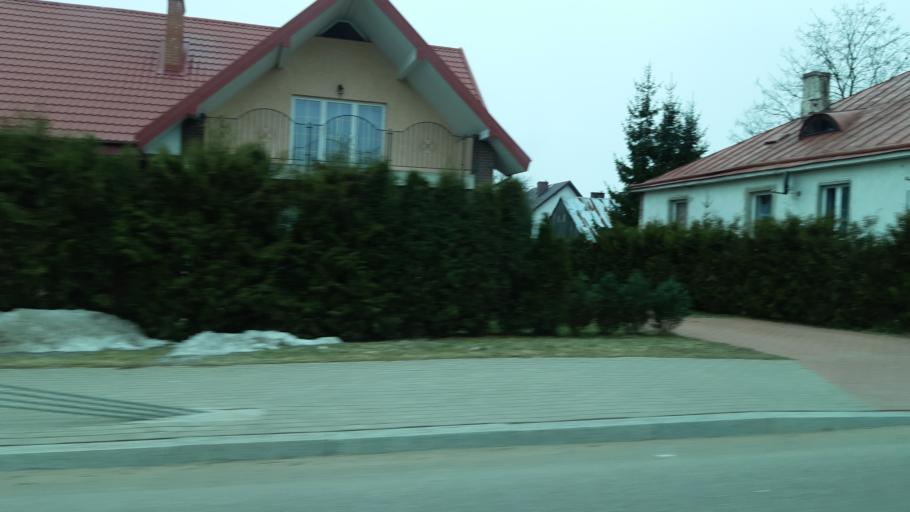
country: PL
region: Podlasie
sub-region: Suwalki
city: Suwalki
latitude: 54.3257
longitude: 22.9676
